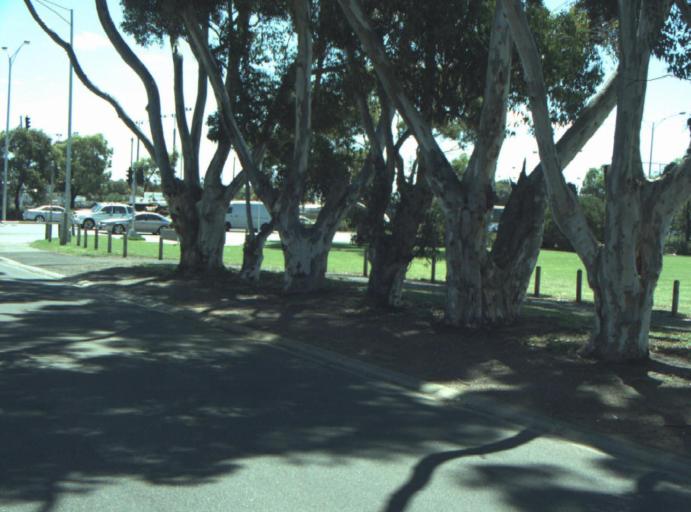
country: AU
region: Victoria
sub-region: Greater Geelong
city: Bell Park
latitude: -38.1198
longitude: 144.3544
